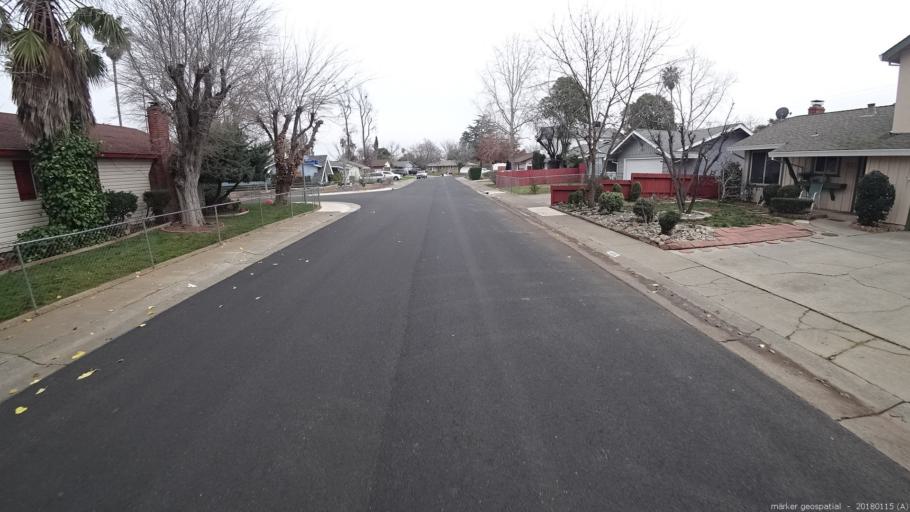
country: US
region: California
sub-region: Sacramento County
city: Rancho Cordova
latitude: 38.5814
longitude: -121.3064
